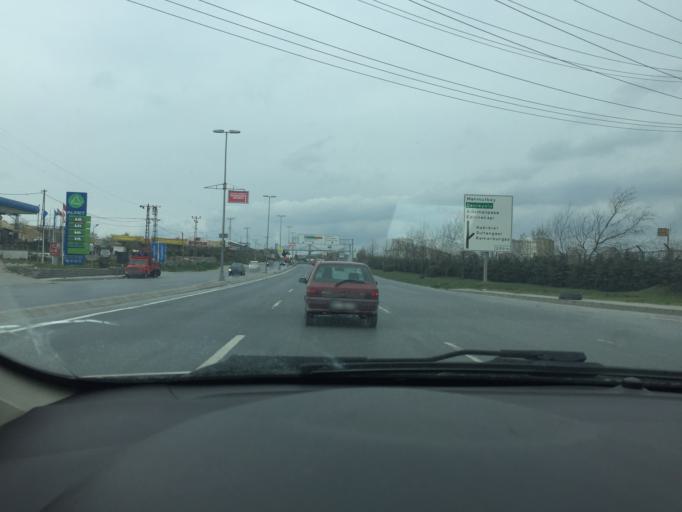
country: TR
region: Istanbul
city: Basaksehir
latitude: 41.1363
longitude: 28.8165
